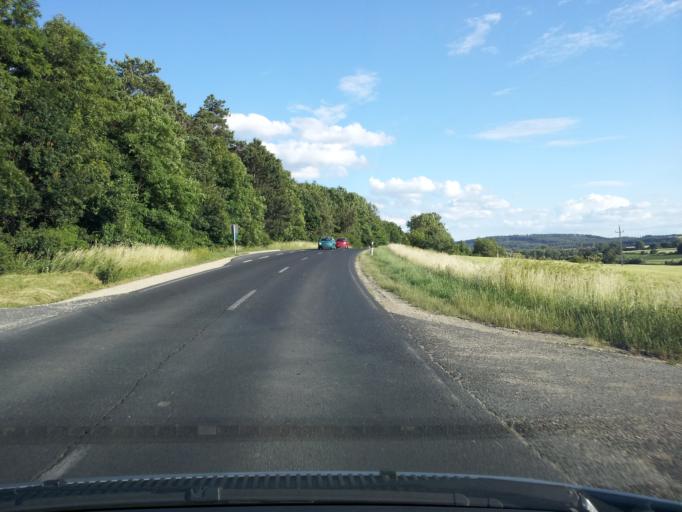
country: HU
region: Veszprem
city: Zirc
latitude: 47.2382
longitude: 17.8986
